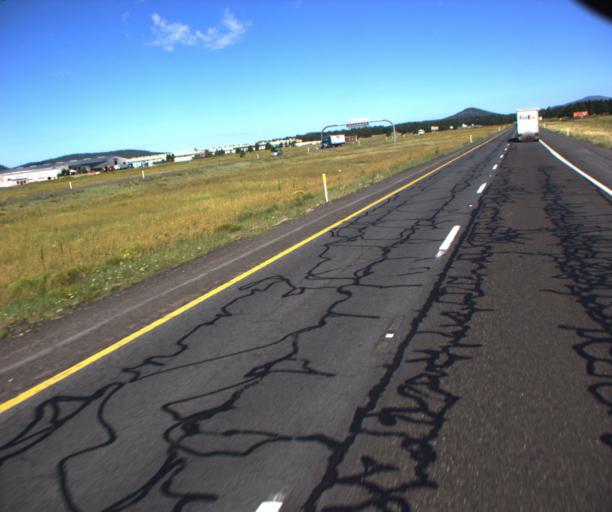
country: US
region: Arizona
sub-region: Coconino County
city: Parks
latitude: 35.2398
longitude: -111.8295
